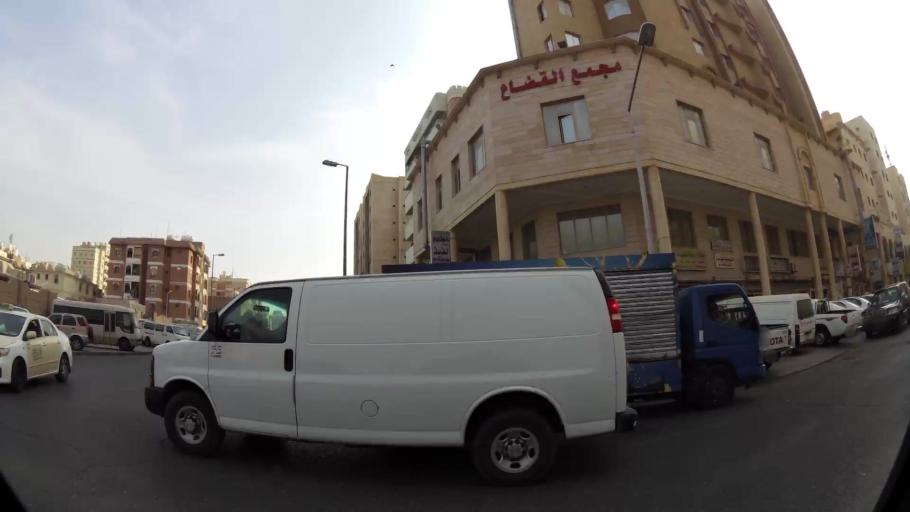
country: KW
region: Al Farwaniyah
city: Al Farwaniyah
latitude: 29.2955
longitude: 47.9740
